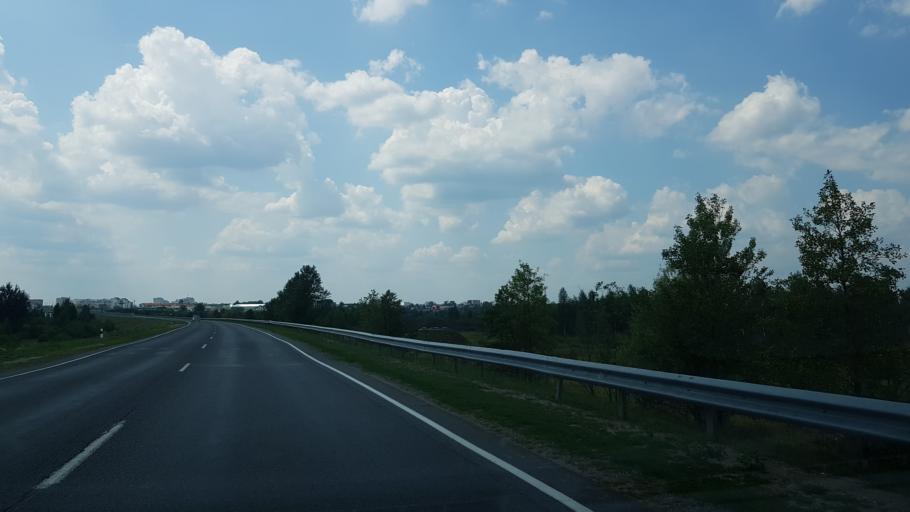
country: BY
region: Mogilev
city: Babruysk
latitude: 53.1674
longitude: 29.2572
